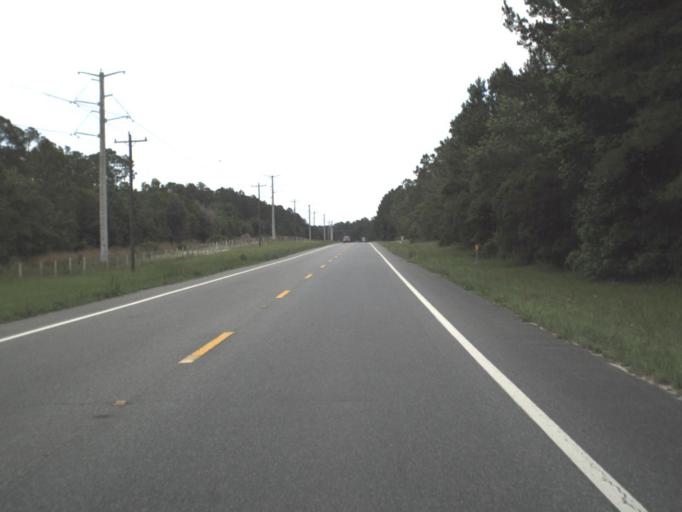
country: US
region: Florida
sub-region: Clay County
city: Keystone Heights
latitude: 29.8915
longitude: -81.9093
